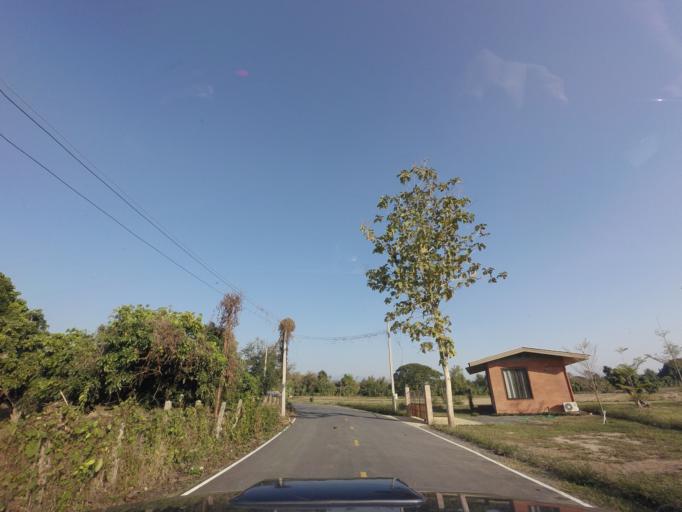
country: TH
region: Chiang Mai
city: San Sai
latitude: 18.9038
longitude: 99.1247
